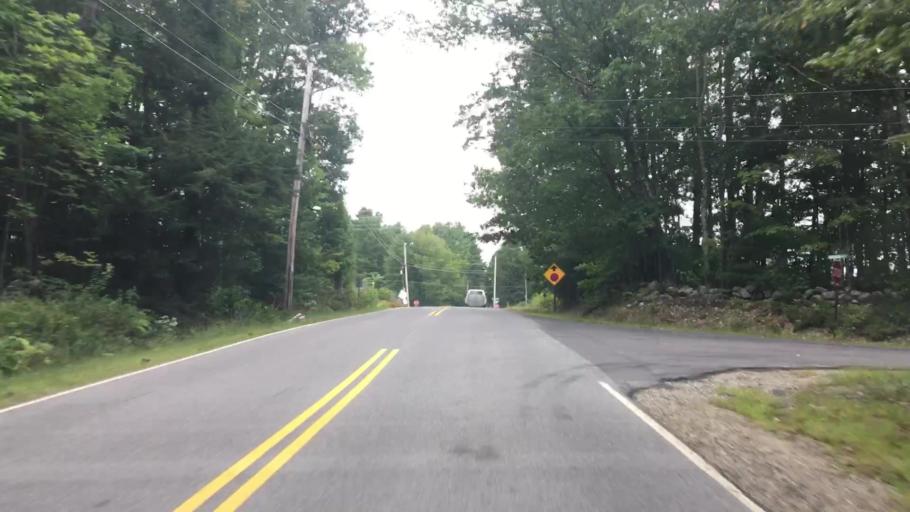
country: US
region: Maine
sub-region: Cumberland County
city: Cumberland Center
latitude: 43.8739
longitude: -70.2416
